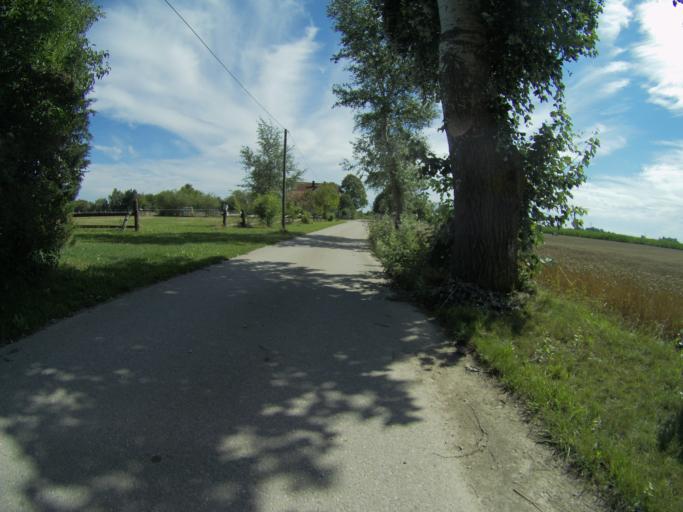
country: DE
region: Bavaria
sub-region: Upper Bavaria
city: Marzling
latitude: 48.4026
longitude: 11.8198
